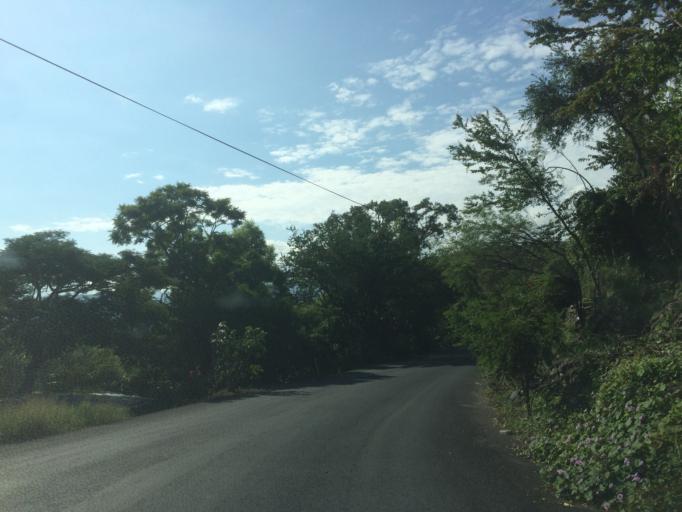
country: MX
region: Nayarit
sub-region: Ahuacatlan
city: Ahuacatlan
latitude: 21.0511
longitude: -104.4746
